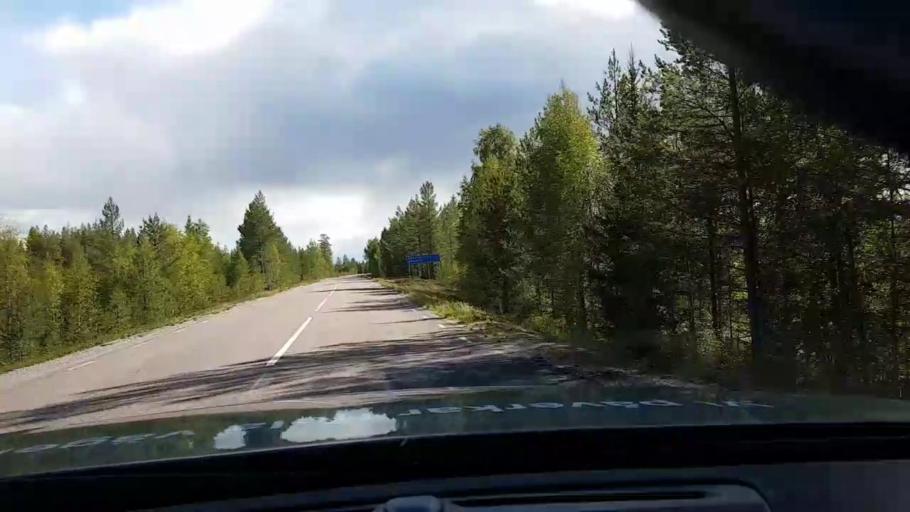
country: SE
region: Vaesterbotten
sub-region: Asele Kommun
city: Asele
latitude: 63.9069
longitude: 17.3420
